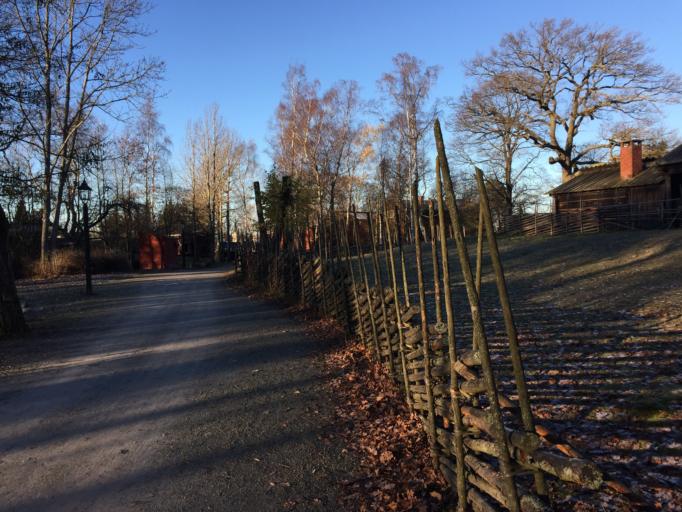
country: SE
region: Stockholm
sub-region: Stockholms Kommun
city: OEstermalm
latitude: 59.3271
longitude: 18.1048
